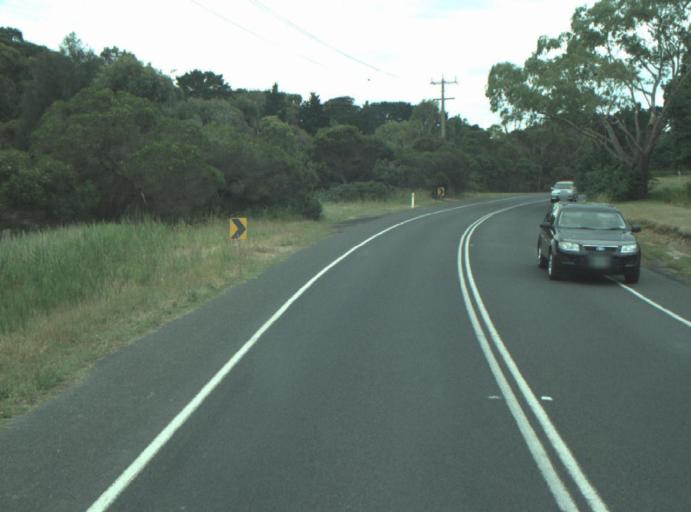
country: AU
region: Victoria
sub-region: Greater Geelong
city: Leopold
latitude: -38.2135
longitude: 144.5069
